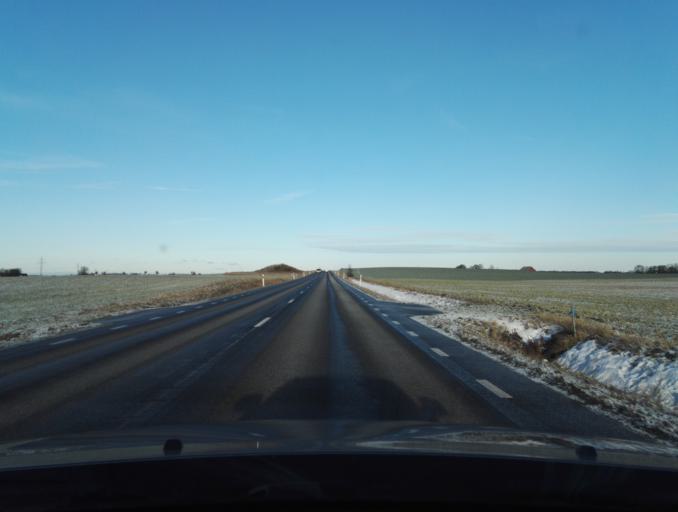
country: SE
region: Skane
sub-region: Trelleborgs Kommun
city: Trelleborg
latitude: 55.4177
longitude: 13.1715
